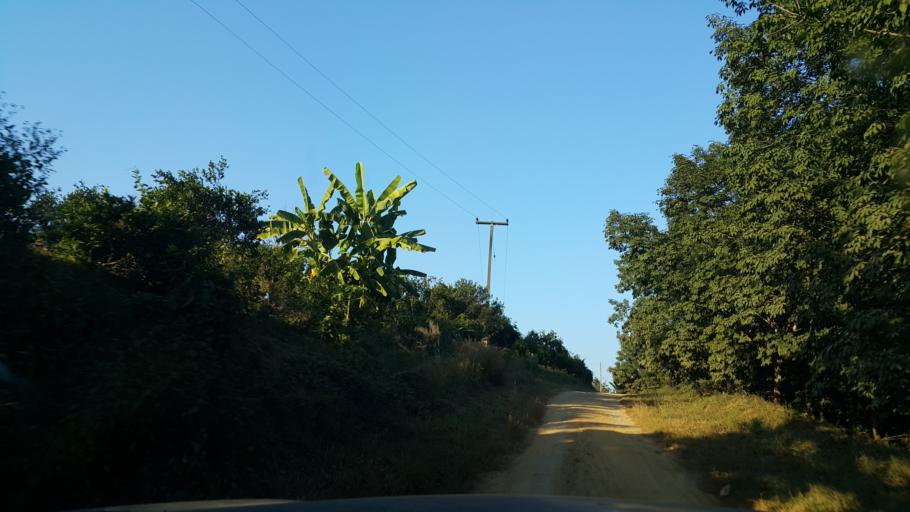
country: TH
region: Sukhothai
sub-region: Amphoe Si Satchanalai
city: Si Satchanalai
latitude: 17.6030
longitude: 99.6142
